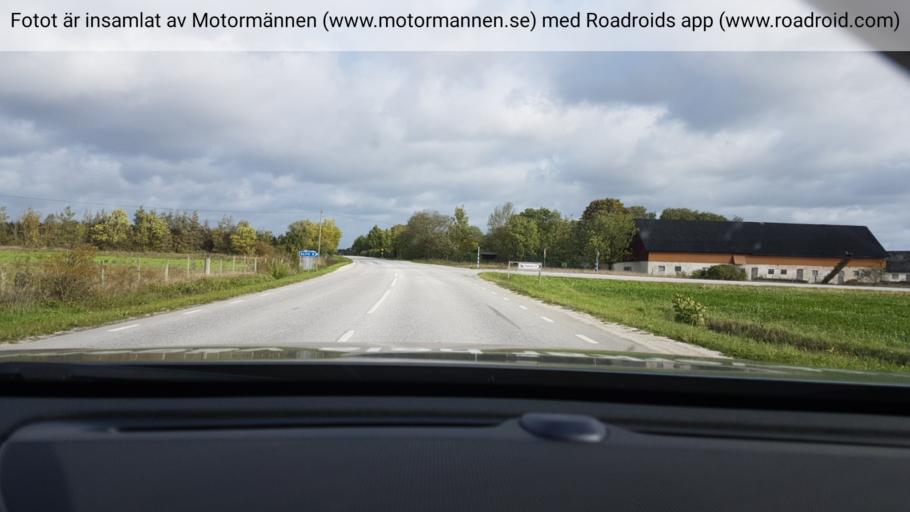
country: SE
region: Gotland
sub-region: Gotland
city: Slite
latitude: 57.7727
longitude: 18.7772
